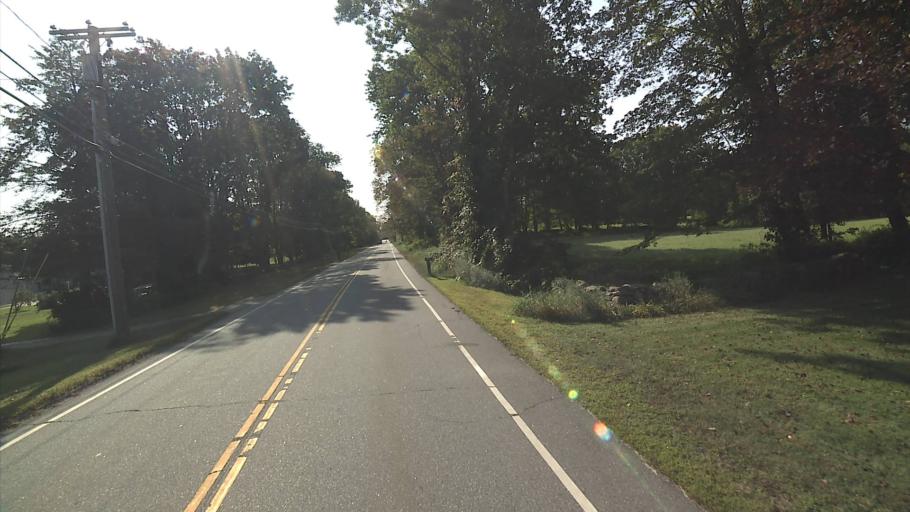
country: US
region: Connecticut
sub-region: Tolland County
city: South Coventry
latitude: 41.6909
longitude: -72.2894
